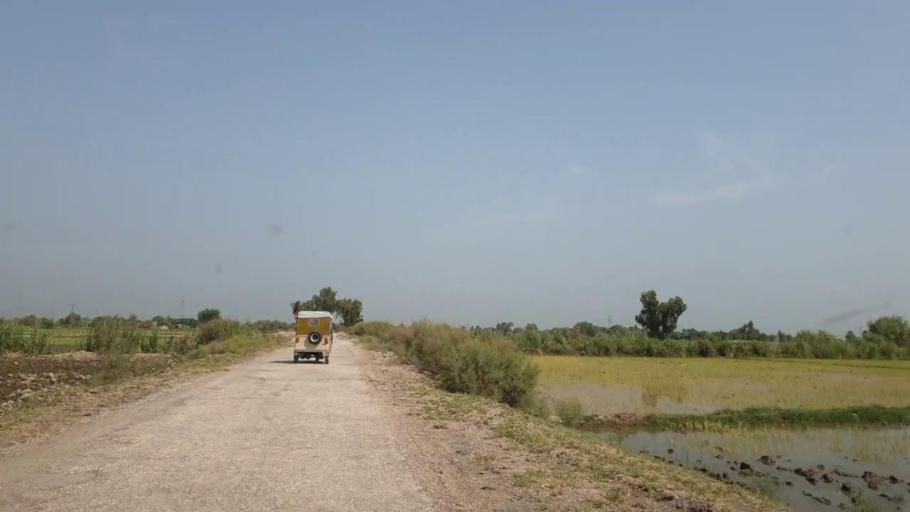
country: PK
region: Sindh
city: Lakhi
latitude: 27.8329
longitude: 68.6823
